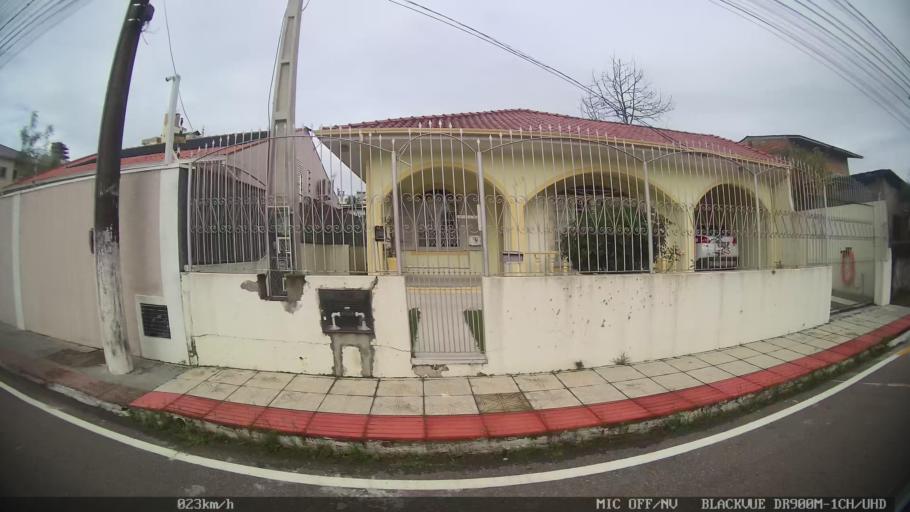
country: BR
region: Santa Catarina
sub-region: Sao Jose
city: Campinas
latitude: -27.5762
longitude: -48.6194
